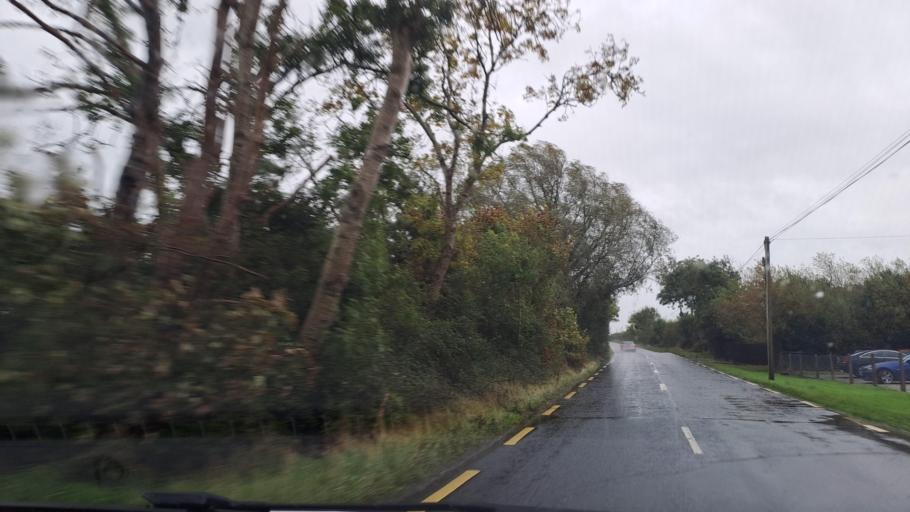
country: GB
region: Northern Ireland
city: Crossmaglen
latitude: 53.9712
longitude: -6.5929
